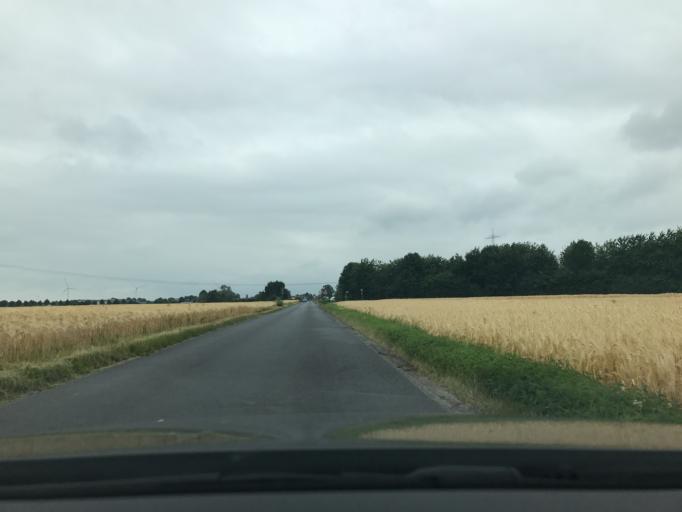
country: DE
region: North Rhine-Westphalia
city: Tonisvorst
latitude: 51.3494
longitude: 6.5126
